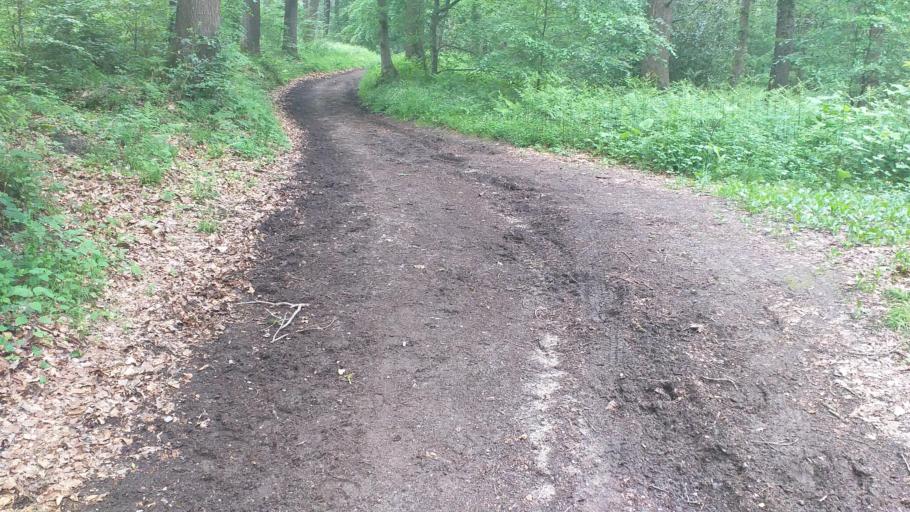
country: DE
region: North Rhine-Westphalia
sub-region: Regierungsbezirk Koln
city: Aachen
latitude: 50.7272
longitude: 6.0774
